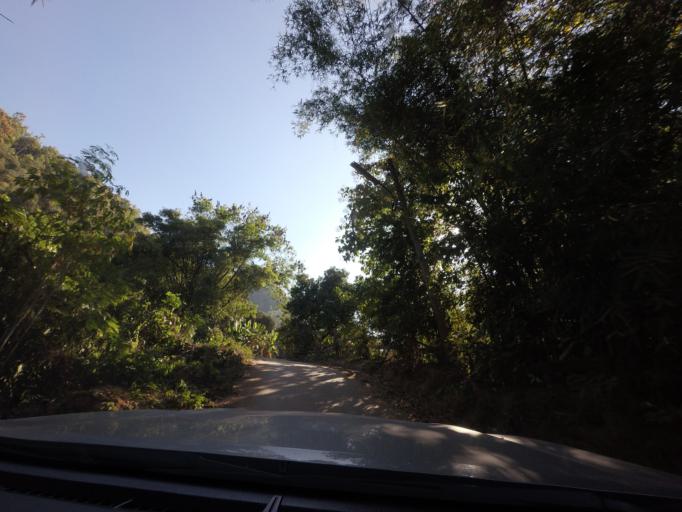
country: TH
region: Lampang
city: Chae Hom
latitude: 18.6162
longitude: 99.6751
